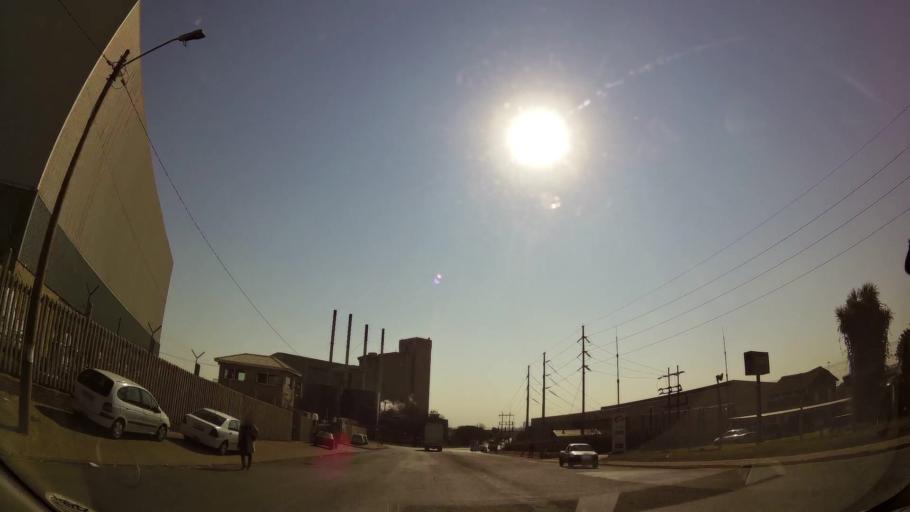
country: ZA
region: Gauteng
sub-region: City of Johannesburg Metropolitan Municipality
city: Modderfontein
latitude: -26.1369
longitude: 28.2150
